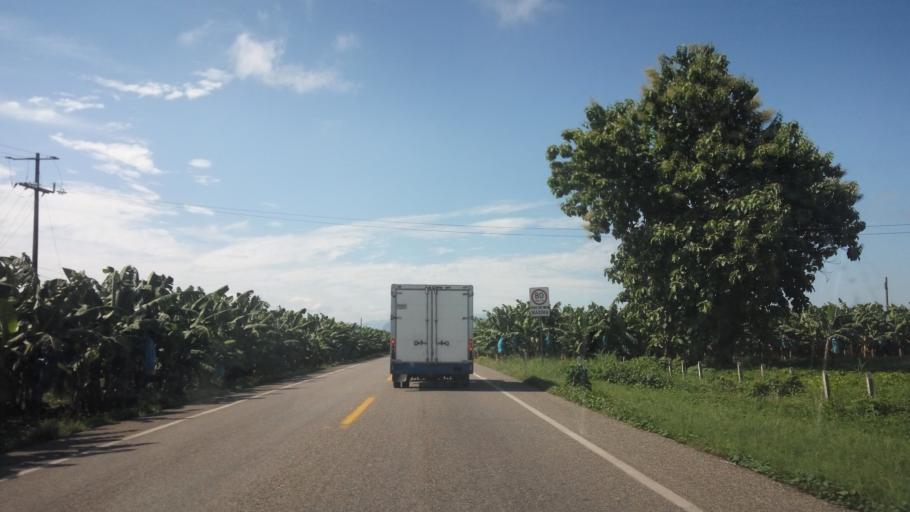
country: MX
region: Tabasco
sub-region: Teapa
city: Eureka y Belen
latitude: 17.6503
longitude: -92.9644
